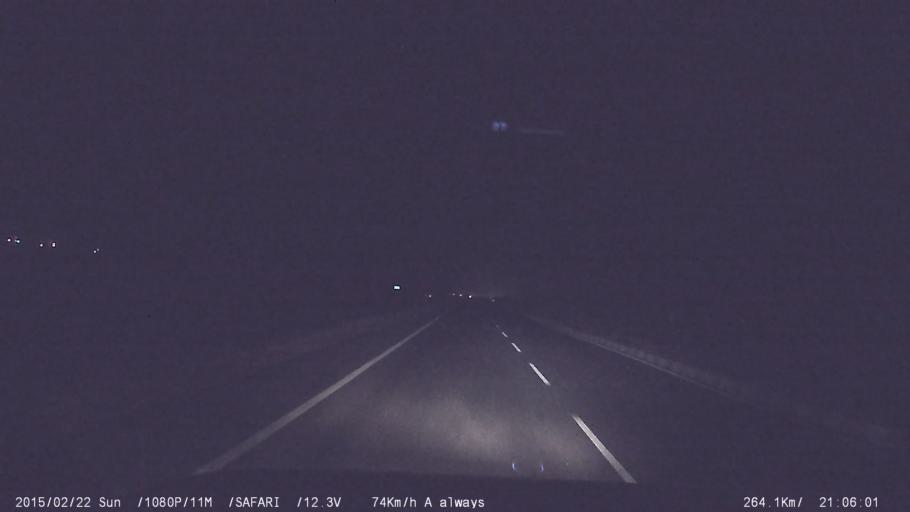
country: IN
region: Tamil Nadu
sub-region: Karur
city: Pallappatti
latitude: 10.7058
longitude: 77.9327
